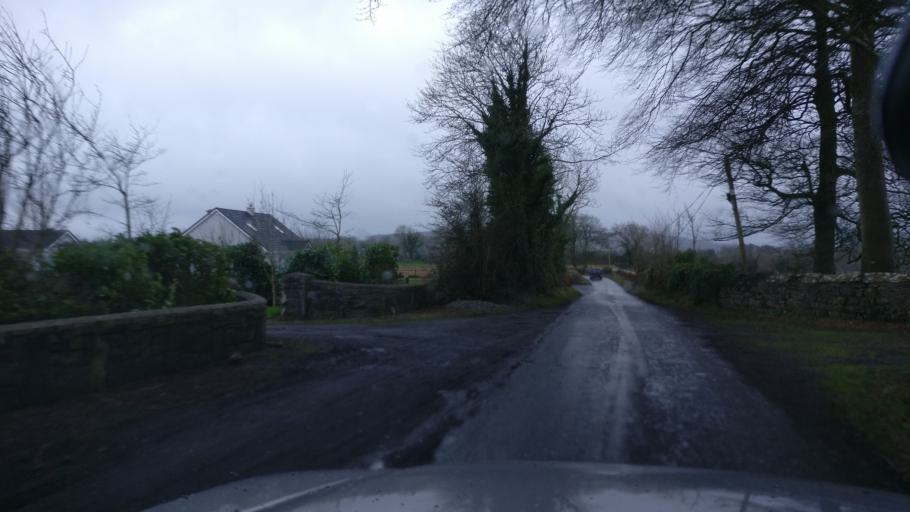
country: IE
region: Connaught
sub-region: County Galway
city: Loughrea
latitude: 53.1952
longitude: -8.6632
